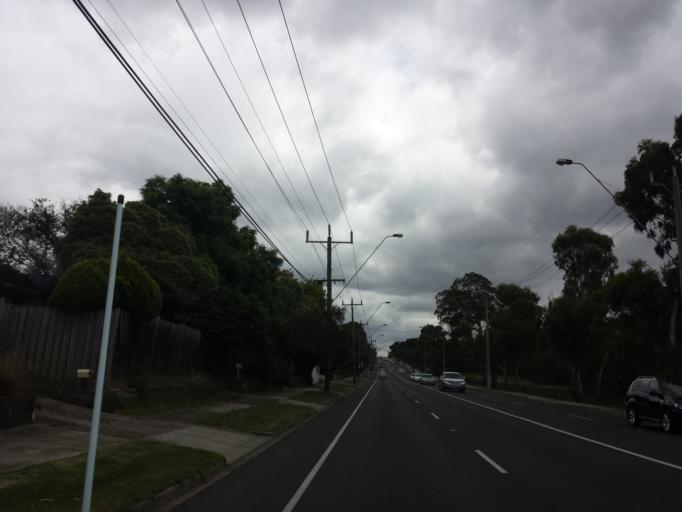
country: AU
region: Victoria
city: Watsonia
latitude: -37.7277
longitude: 145.0798
